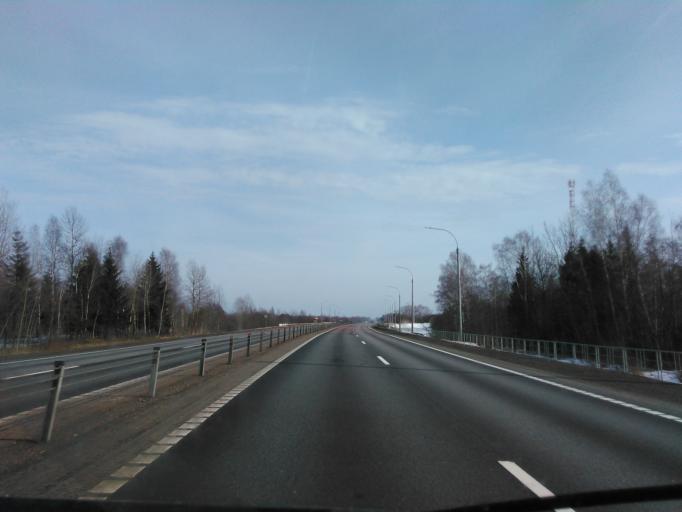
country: BY
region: Vitebsk
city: Dubrowna
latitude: 54.6892
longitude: 30.8837
